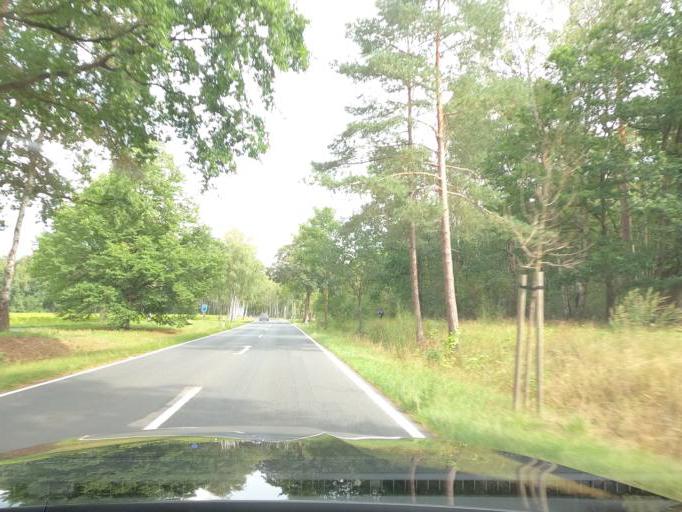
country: DE
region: Lower Saxony
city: Burgdorf
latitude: 52.5038
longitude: 9.9656
